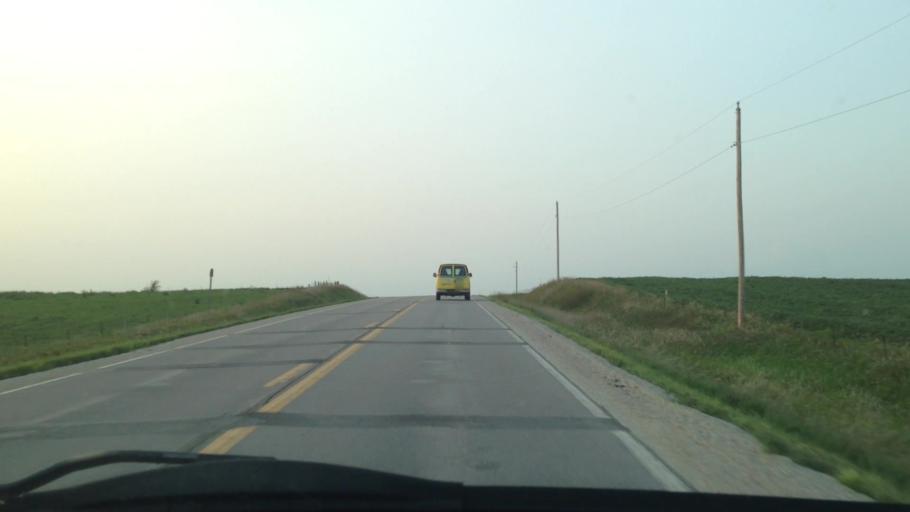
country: US
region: Iowa
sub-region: Benton County
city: Atkins
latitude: 42.0129
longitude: -91.8737
